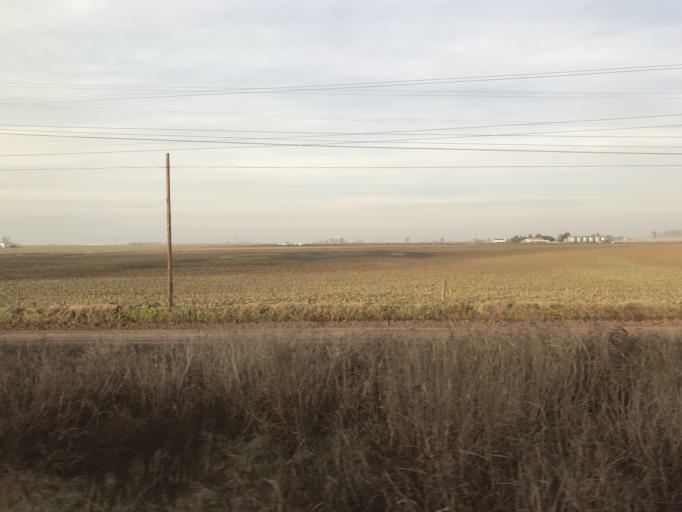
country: AR
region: Cordoba
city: Marcos Juarez
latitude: -32.6833
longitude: -62.1952
